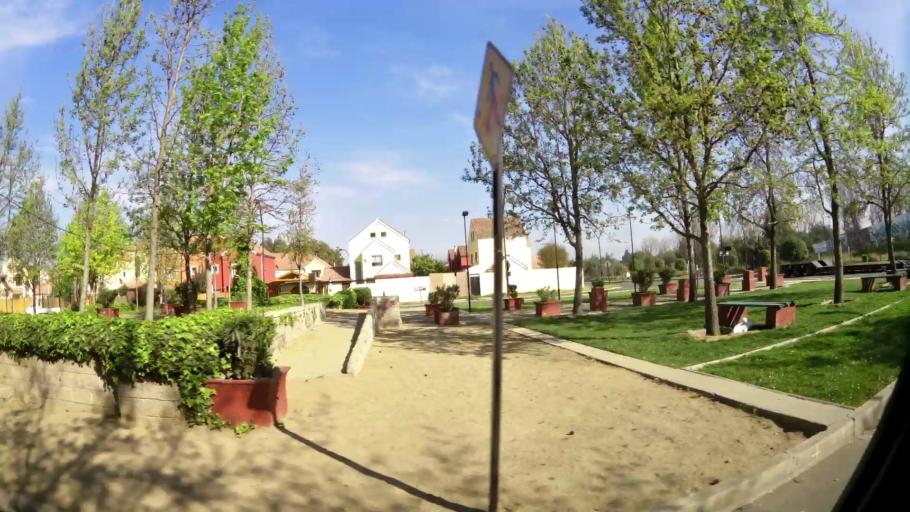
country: CL
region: Santiago Metropolitan
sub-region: Provincia de Santiago
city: Lo Prado
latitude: -33.4506
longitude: -70.7600
